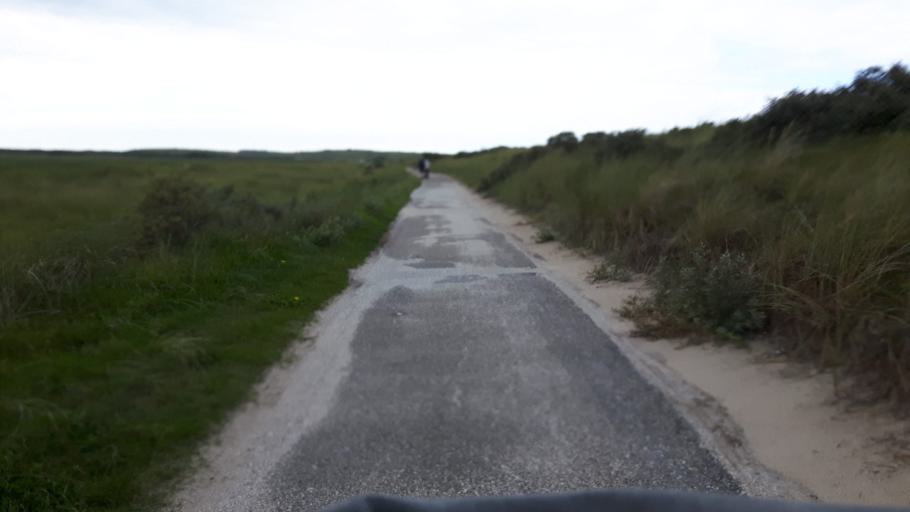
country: NL
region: Friesland
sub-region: Gemeente Ameland
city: Nes
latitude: 53.4612
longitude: 5.8434
